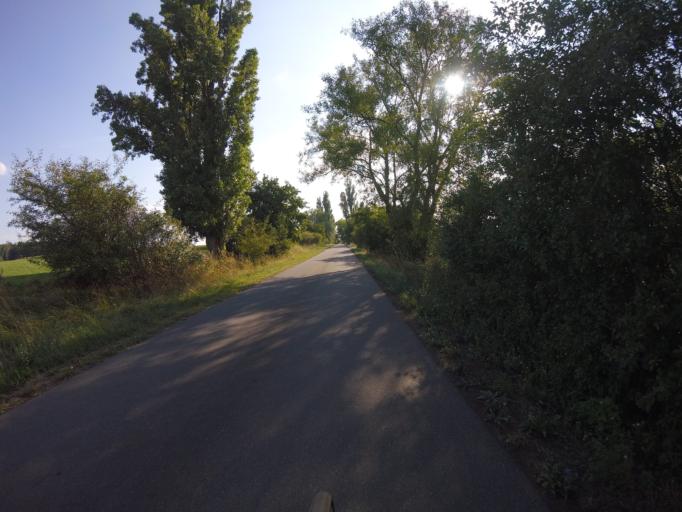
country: DE
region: Brandenburg
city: Bliesdorf
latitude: 52.6681
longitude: 14.1257
